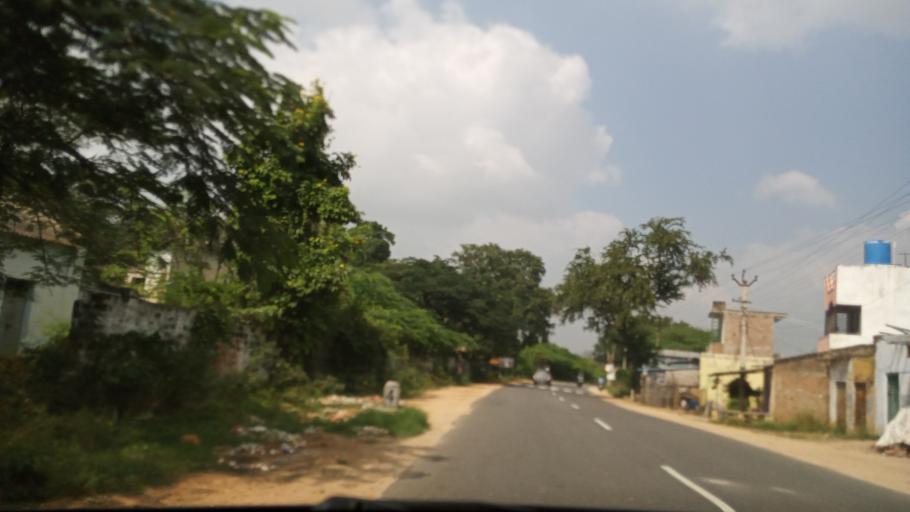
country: IN
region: Andhra Pradesh
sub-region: Chittoor
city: Madanapalle
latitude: 13.6354
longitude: 78.5545
